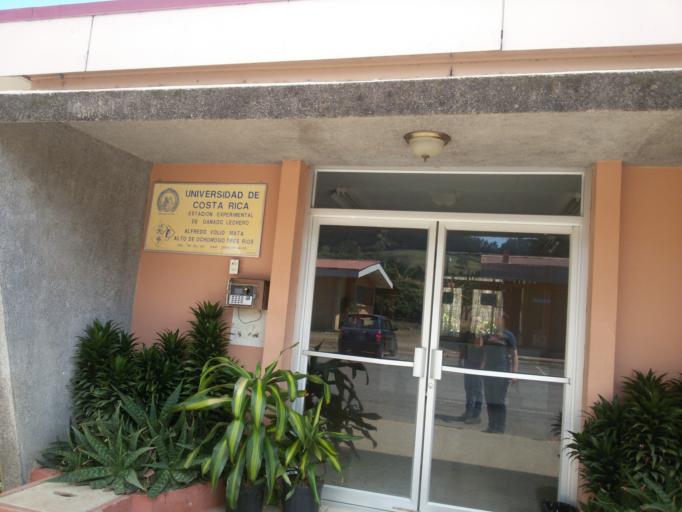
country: CR
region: Cartago
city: Tres Rios
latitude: 9.9119
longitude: -83.9548
